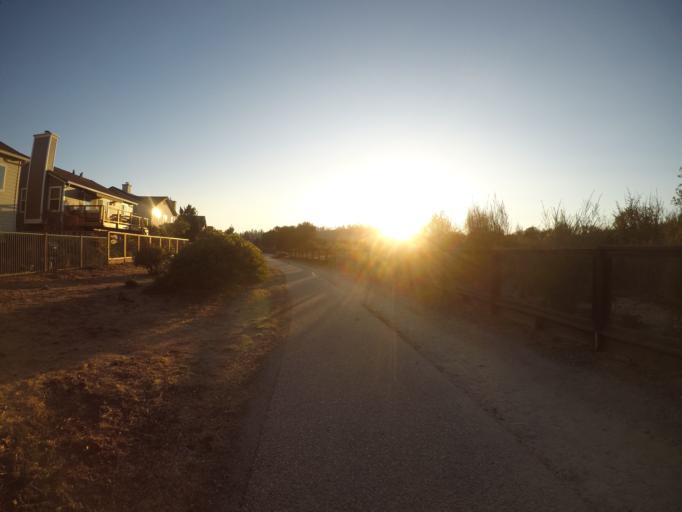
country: US
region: California
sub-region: Santa Cruz County
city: Scotts Valley
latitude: 37.0535
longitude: -122.0334
